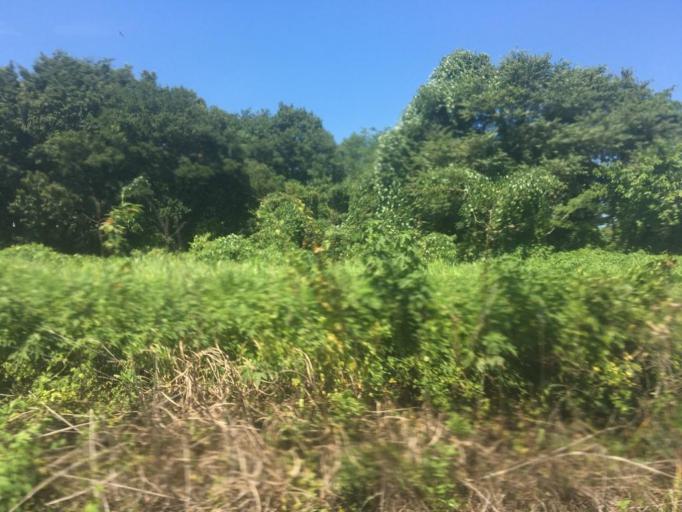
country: JP
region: Saitama
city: Chichibu
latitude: 36.0398
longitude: 139.0996
